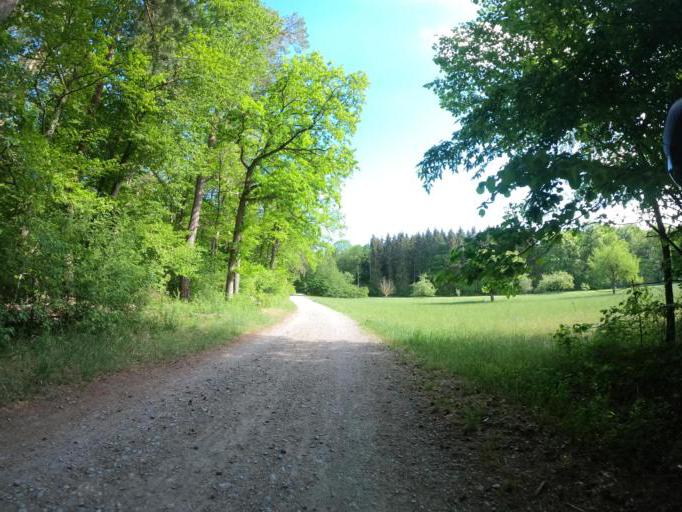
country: DE
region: Baden-Wuerttemberg
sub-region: Regierungsbezirk Stuttgart
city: Aidlingen
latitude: 48.6986
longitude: 8.9124
